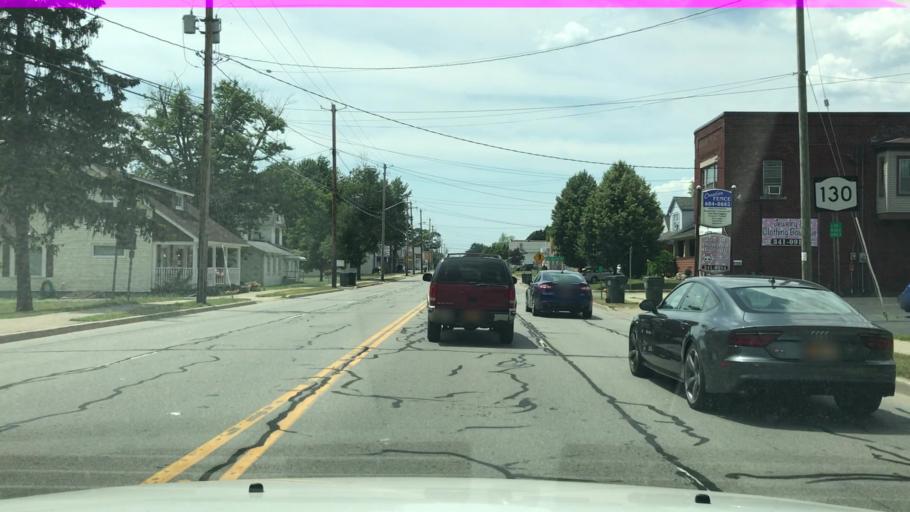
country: US
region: New York
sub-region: Erie County
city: Depew
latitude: 42.9019
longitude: -78.6985
